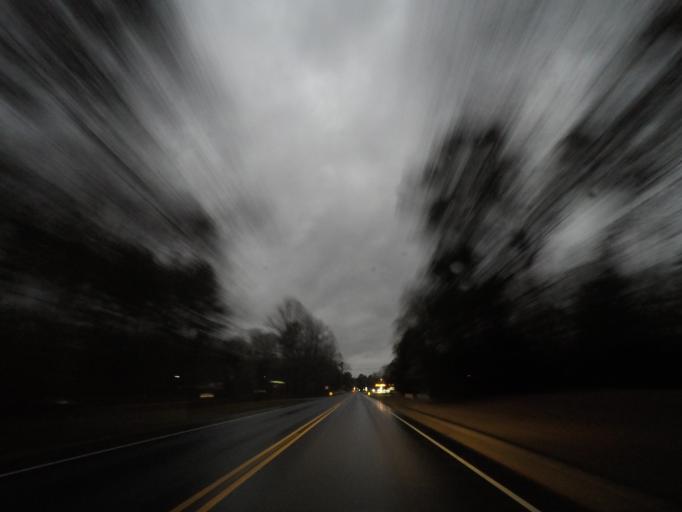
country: US
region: North Carolina
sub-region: Orange County
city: Hillsborough
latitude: 36.0774
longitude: -79.0732
